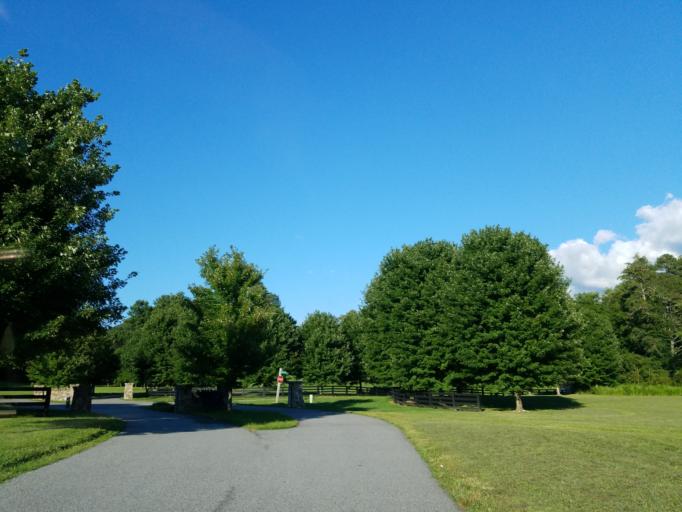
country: US
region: Georgia
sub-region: Union County
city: Blairsville
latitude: 34.7616
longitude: -84.1052
